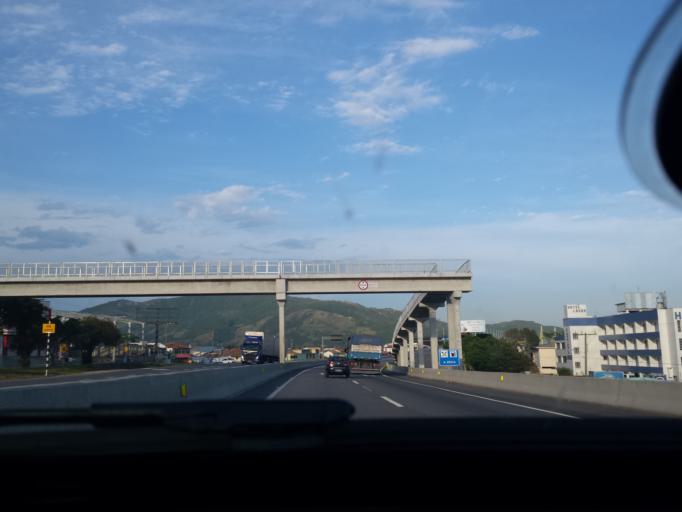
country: BR
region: Santa Catarina
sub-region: Laguna
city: Laguna
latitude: -28.4410
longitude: -48.8207
